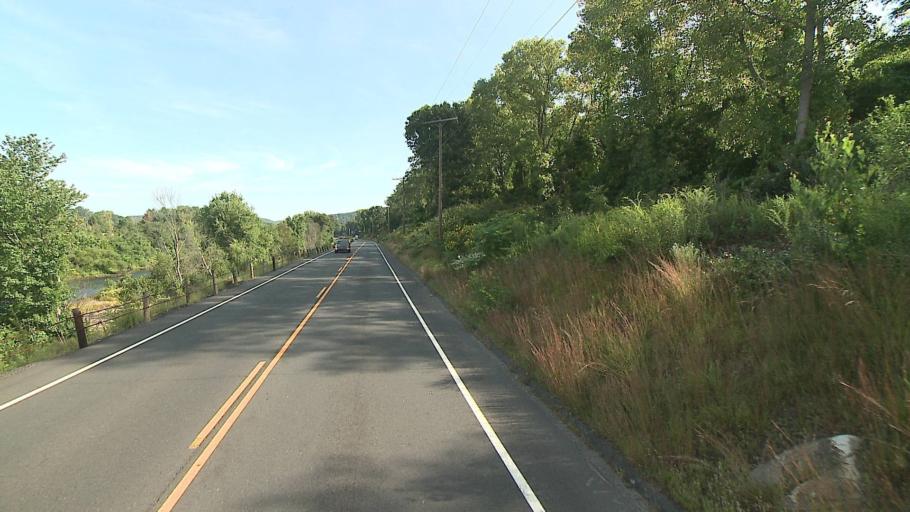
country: US
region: Connecticut
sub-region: New Haven County
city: Waterbury
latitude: 41.5736
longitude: -73.0521
